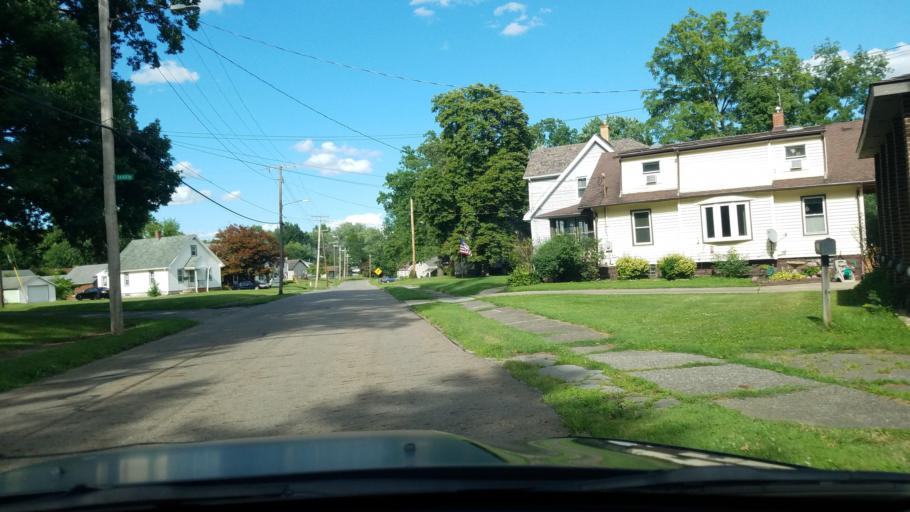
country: US
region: Ohio
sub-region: Trumbull County
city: Niles
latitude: 41.1707
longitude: -80.7775
